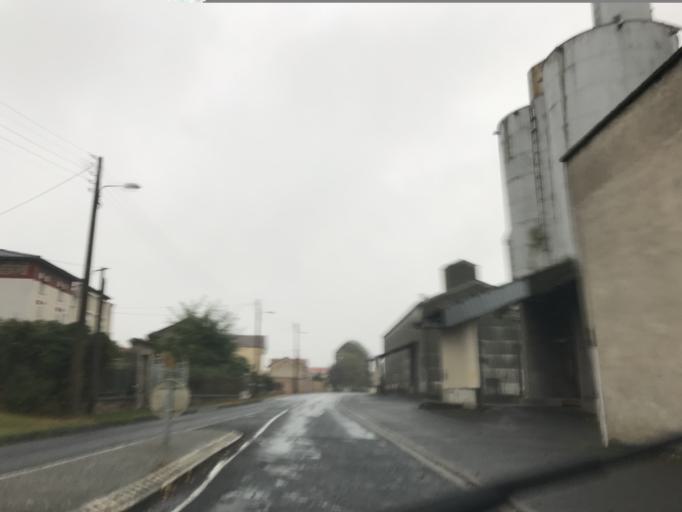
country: FR
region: Auvergne
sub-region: Departement du Puy-de-Dome
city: Vertaizon
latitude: 45.7853
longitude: 3.2891
